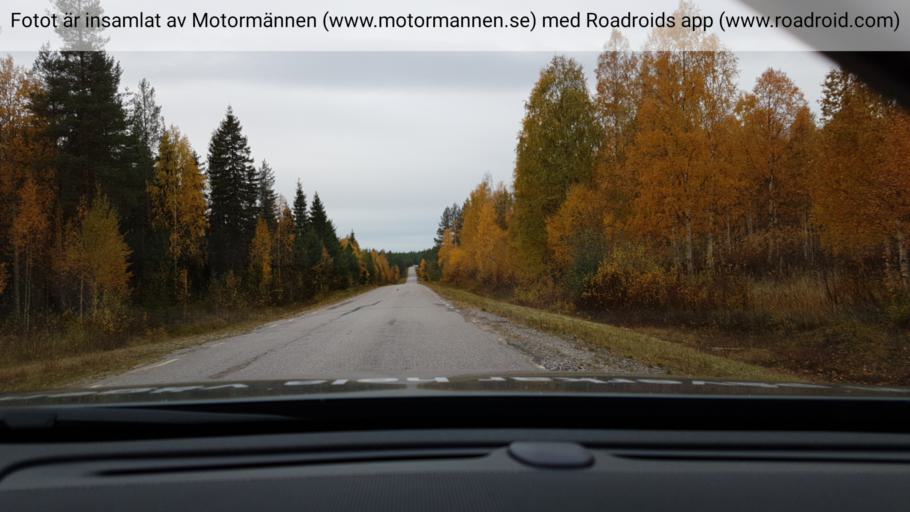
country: SE
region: Norrbotten
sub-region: Overkalix Kommun
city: OEverkalix
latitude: 66.2372
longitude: 22.9663
